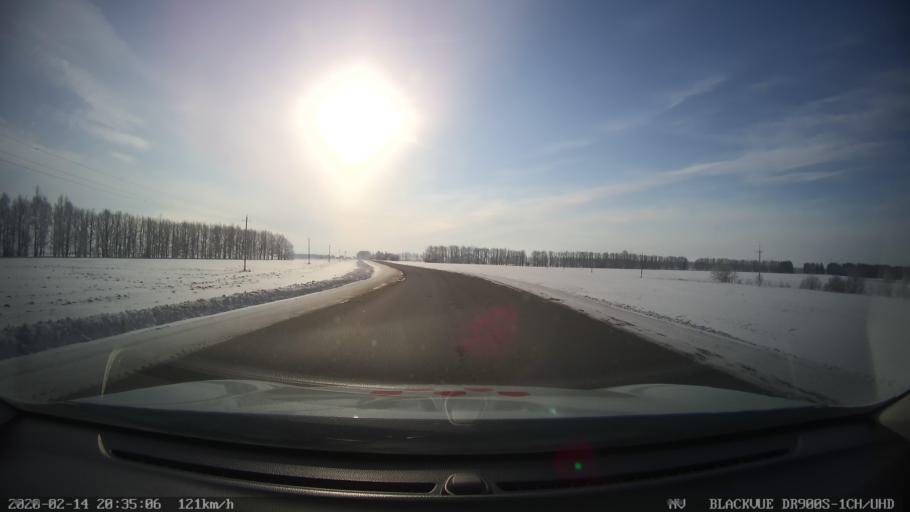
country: RU
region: Tatarstan
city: Kuybyshevskiy Zaton
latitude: 55.3874
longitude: 48.9802
